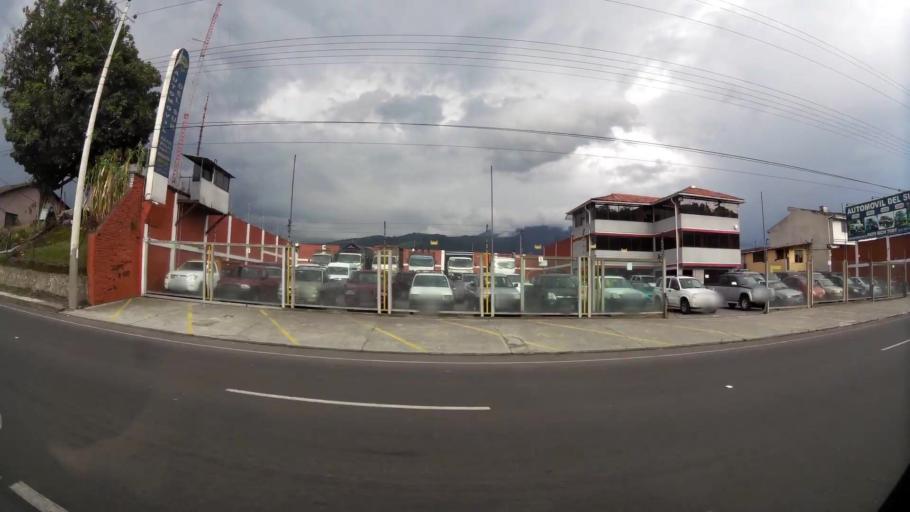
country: EC
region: Pichincha
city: Machachi
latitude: -0.4034
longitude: -78.5457
